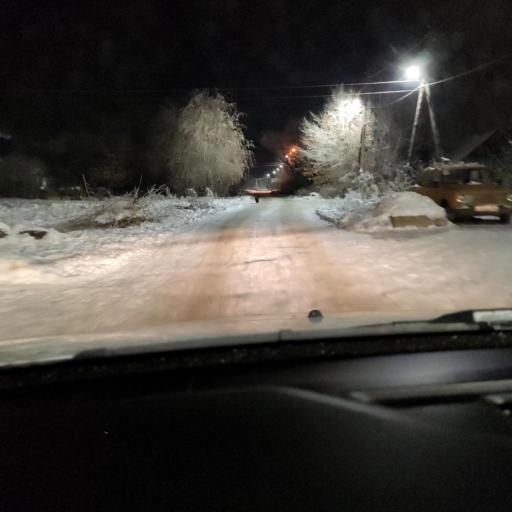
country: RU
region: Samara
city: Petra-Dubrava
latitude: 53.2420
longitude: 50.3134
